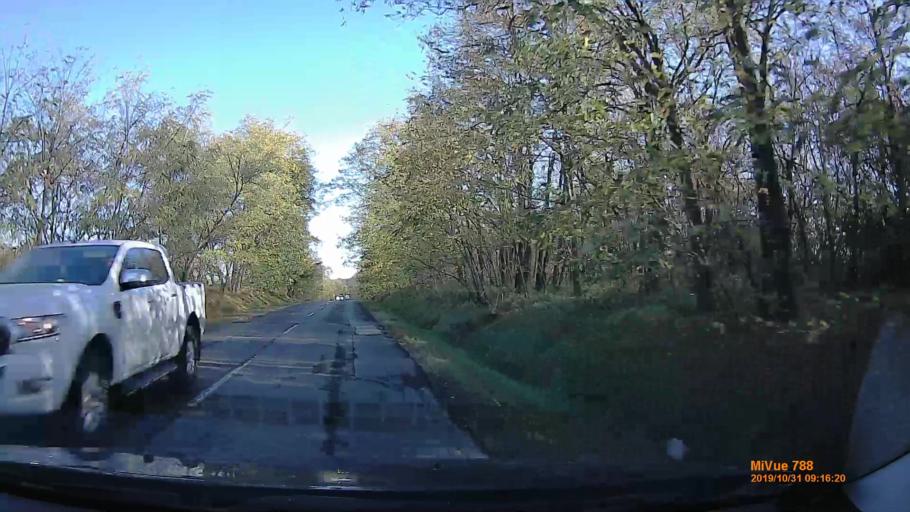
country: HU
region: Pest
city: Peteri
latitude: 47.4007
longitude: 19.4095
